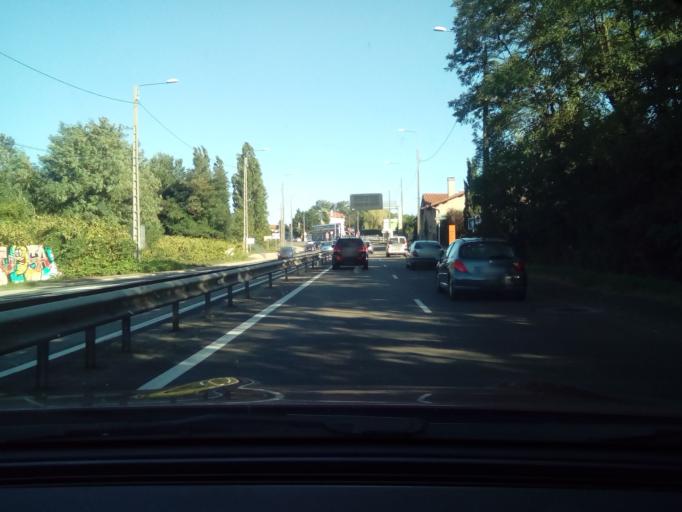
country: FR
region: Rhone-Alpes
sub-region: Departement du Rhone
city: Limonest
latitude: 45.8258
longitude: 4.7582
